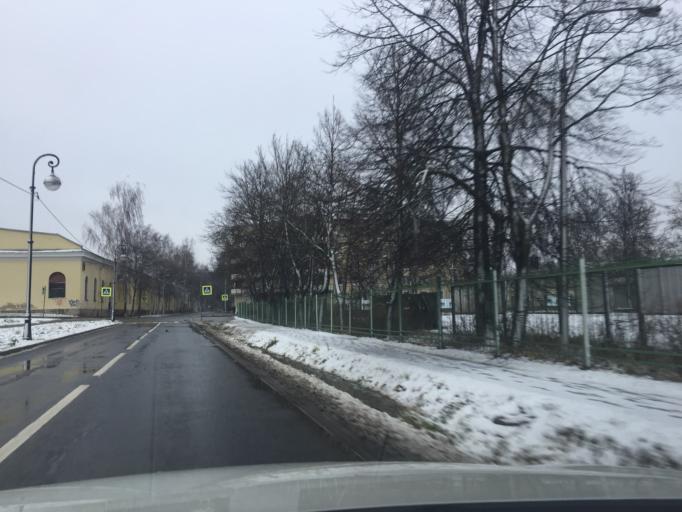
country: RU
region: St.-Petersburg
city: Pushkin
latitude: 59.7059
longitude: 30.3955
